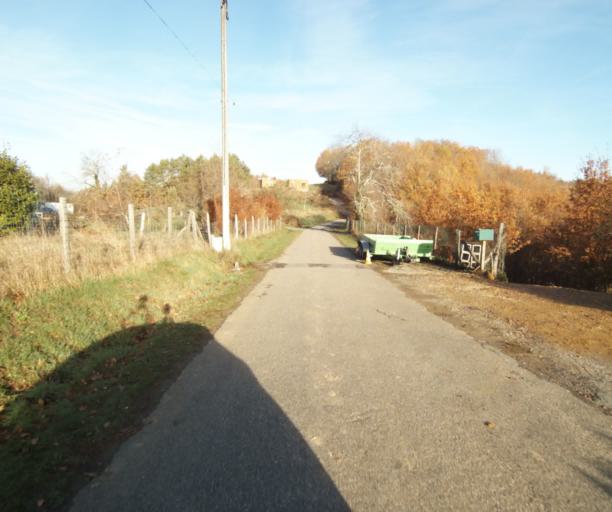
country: FR
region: Limousin
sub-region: Departement de la Correze
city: Laguenne
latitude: 45.2581
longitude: 1.7989
